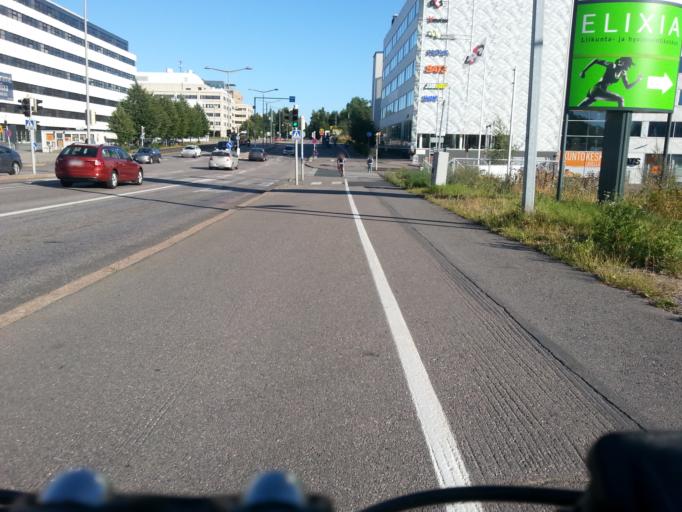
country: FI
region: Uusimaa
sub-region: Helsinki
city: Teekkarikylae
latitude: 60.2154
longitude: 24.8746
